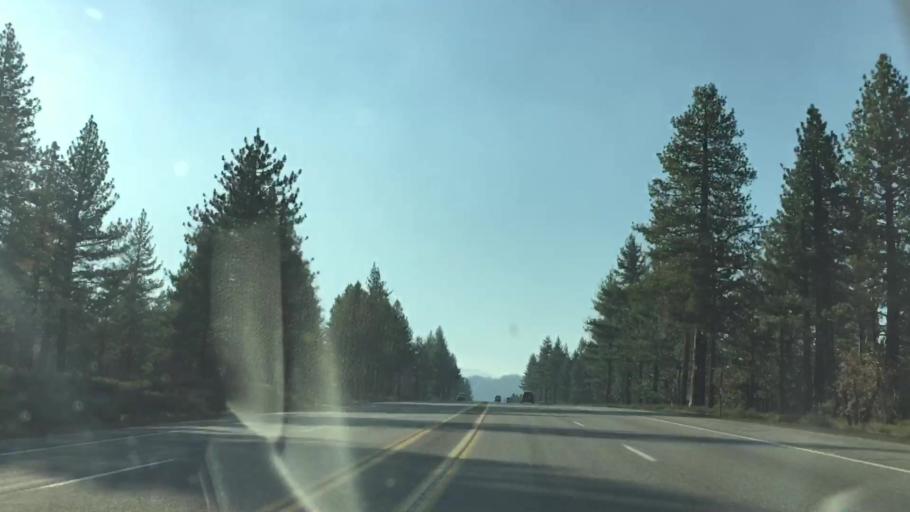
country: US
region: California
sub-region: Mono County
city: Mammoth Lakes
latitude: 37.7685
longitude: -119.0044
